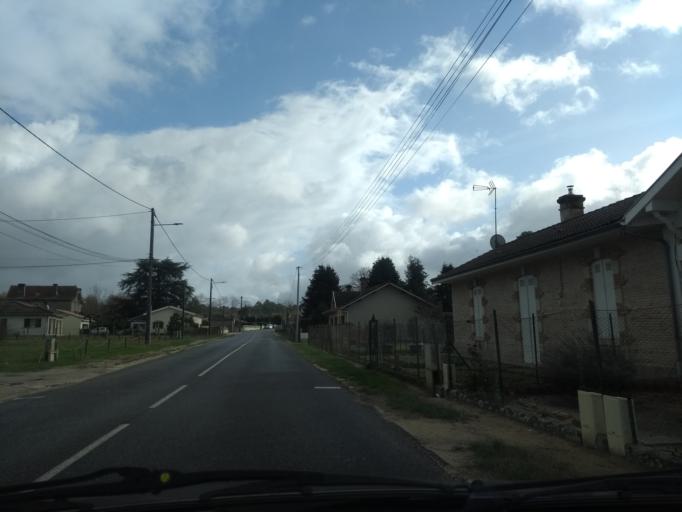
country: FR
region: Aquitaine
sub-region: Departement de la Gironde
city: Belin-Beliet
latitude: 44.4924
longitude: -0.7860
